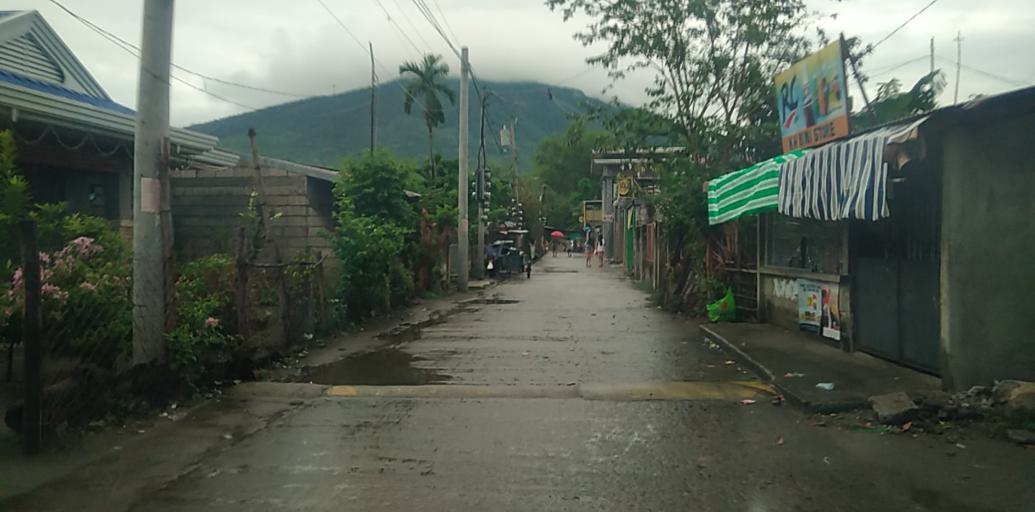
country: PH
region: Central Luzon
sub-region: Province of Pampanga
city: Arayat
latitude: 15.1548
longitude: 120.7391
